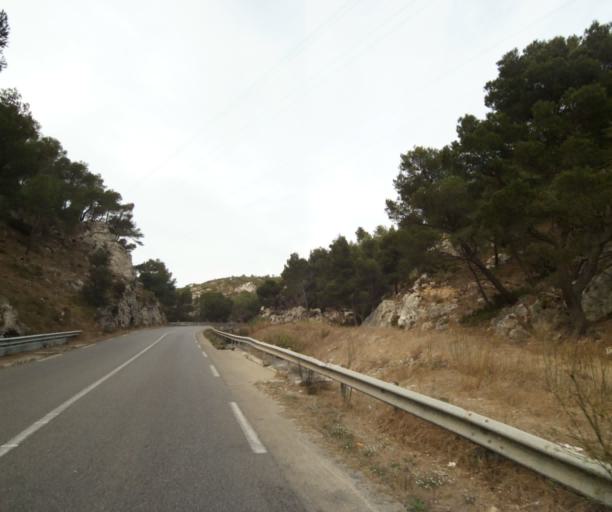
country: FR
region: Provence-Alpes-Cote d'Azur
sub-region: Departement des Bouches-du-Rhone
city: Le Rove
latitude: 43.3641
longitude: 5.2655
